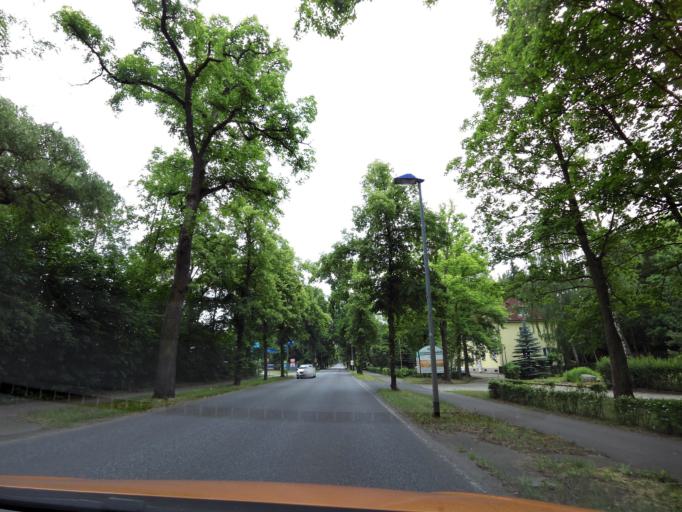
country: DE
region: Brandenburg
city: Zossen
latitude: 52.1718
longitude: 13.4704
